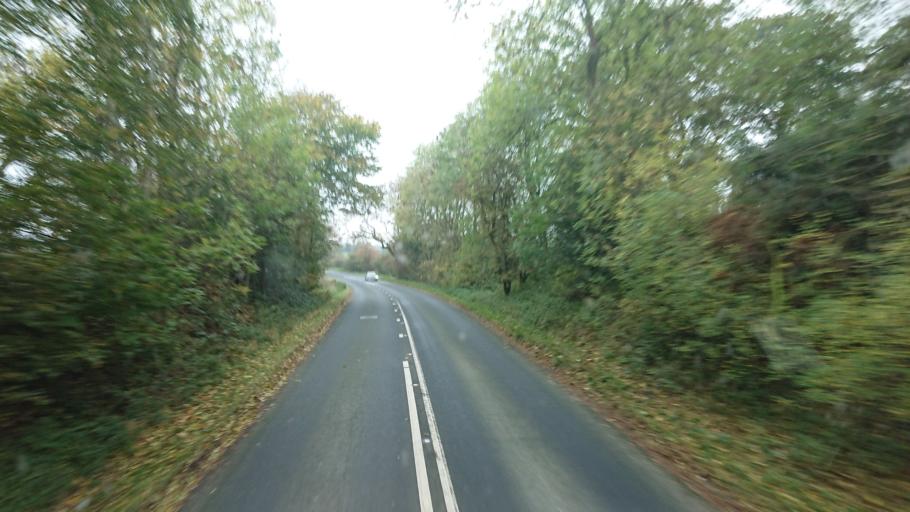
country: GB
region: England
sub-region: North Yorkshire
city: Skipton
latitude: 54.0272
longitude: -2.0453
